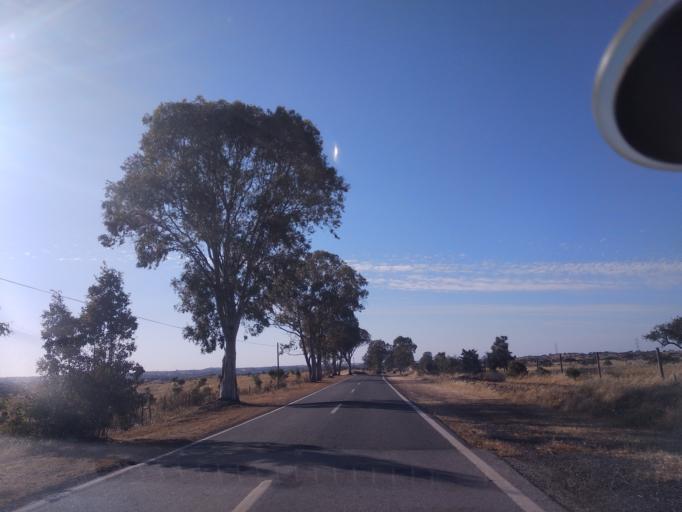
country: PT
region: Beja
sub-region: Almodovar
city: Almodovar
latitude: 37.4556
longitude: -7.9985
